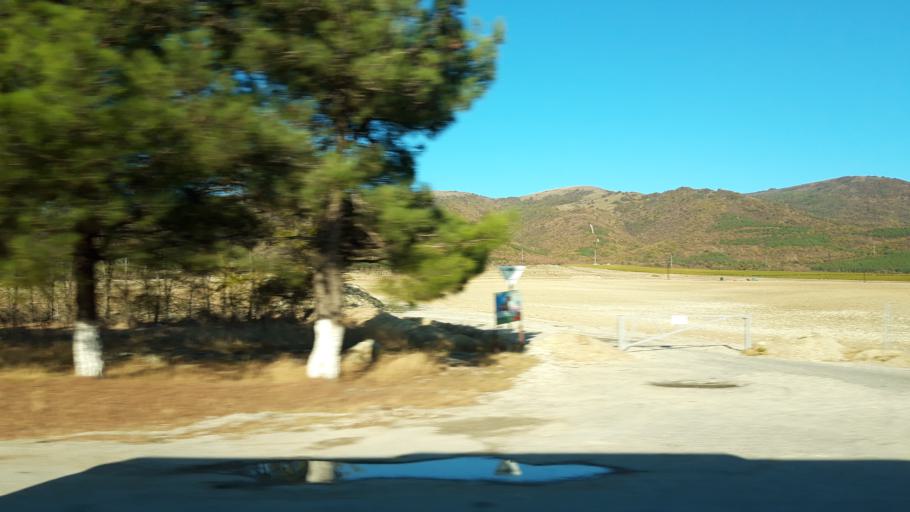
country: RU
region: Krasnodarskiy
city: Kabardinka
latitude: 44.6300
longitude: 38.0032
